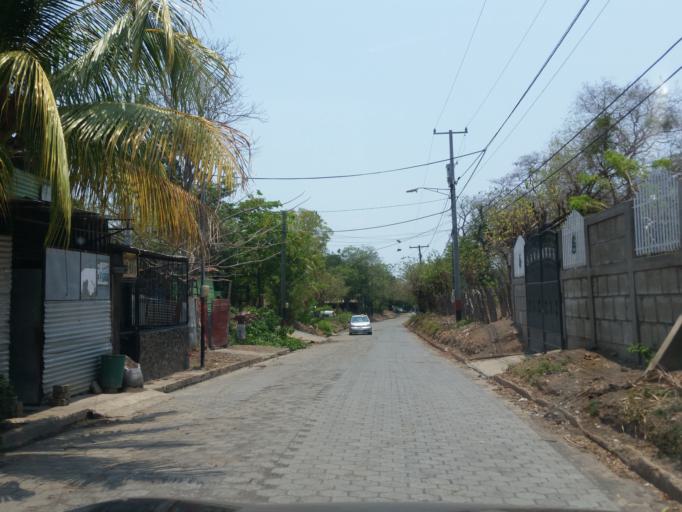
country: NI
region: Granada
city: Granada
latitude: 11.9295
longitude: -85.9689
